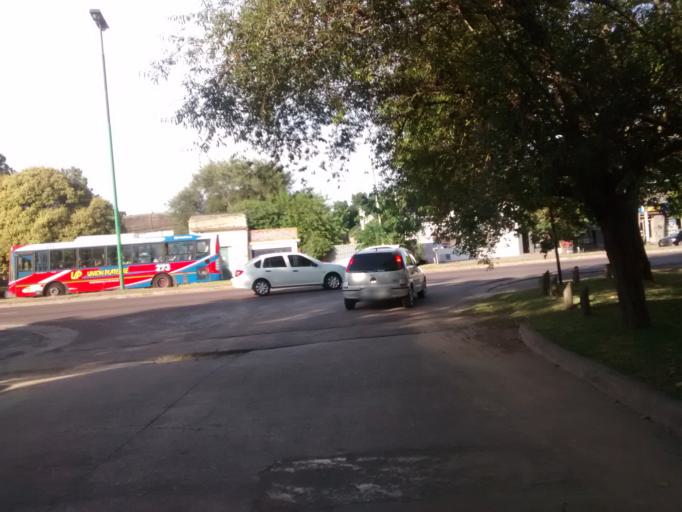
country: AR
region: Buenos Aires
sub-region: Partido de La Plata
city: La Plata
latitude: -34.8547
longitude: -58.0774
